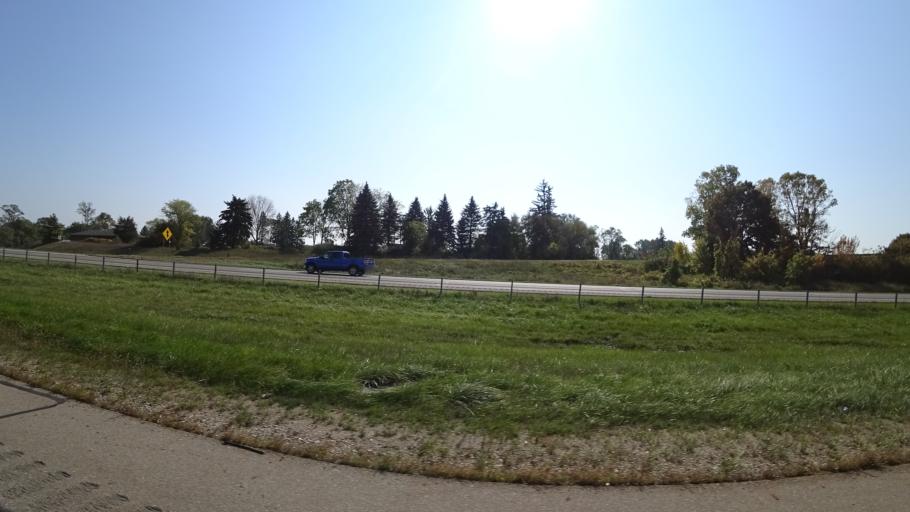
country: US
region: Michigan
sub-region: Washtenaw County
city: Chelsea
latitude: 42.2981
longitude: -83.9724
